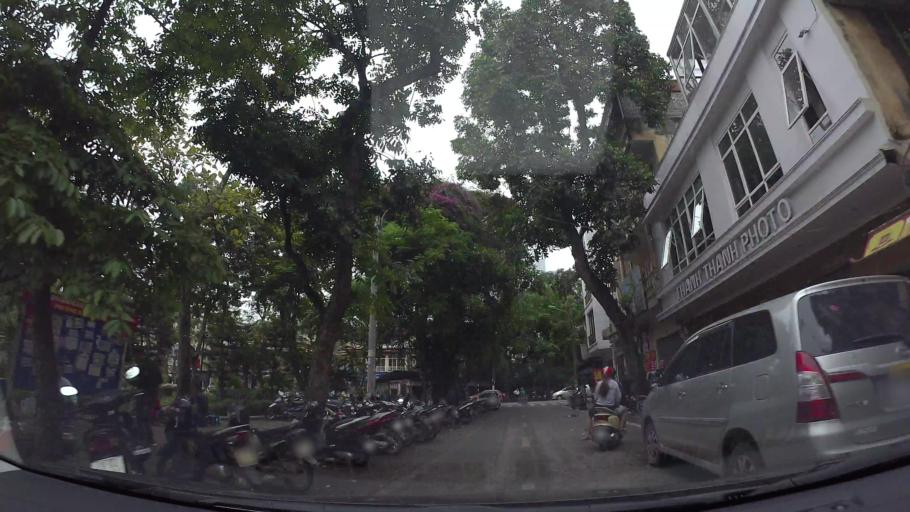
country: VN
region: Ha Noi
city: Hai BaTrung
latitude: 21.0131
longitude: 105.8611
